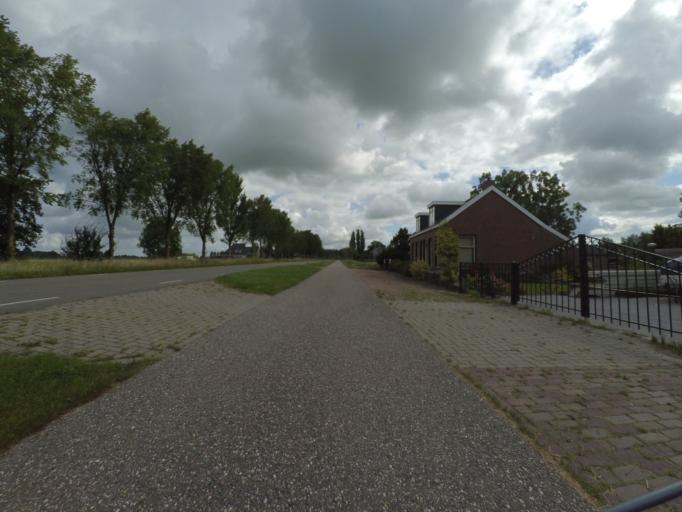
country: NL
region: Friesland
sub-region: Gemeente Achtkarspelen
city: Buitenpost
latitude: 53.2568
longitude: 6.1604
